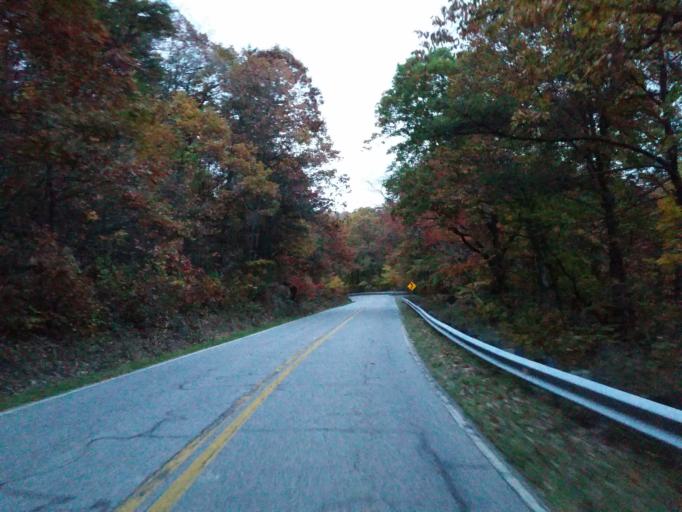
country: US
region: Georgia
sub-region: Lumpkin County
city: Dahlonega
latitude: 34.6726
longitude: -83.9891
